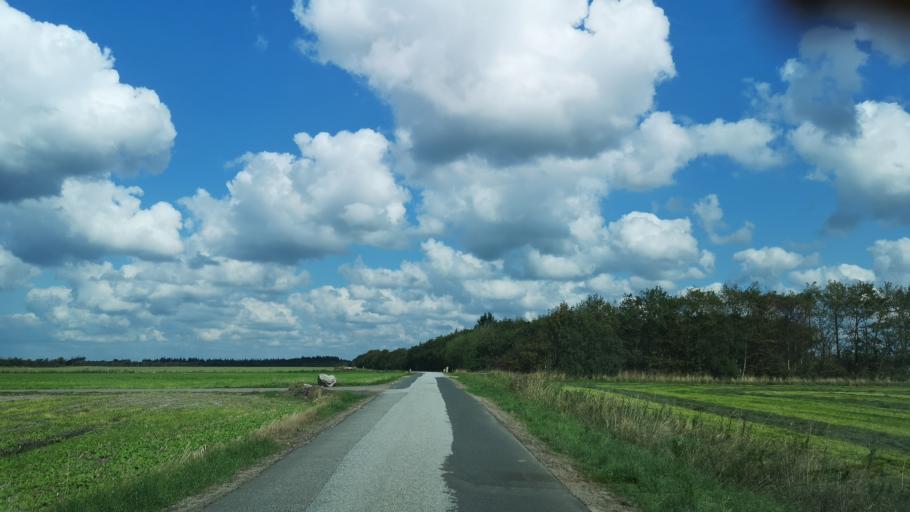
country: DK
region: Central Jutland
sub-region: Ringkobing-Skjern Kommune
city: Skjern
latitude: 55.8538
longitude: 8.3852
